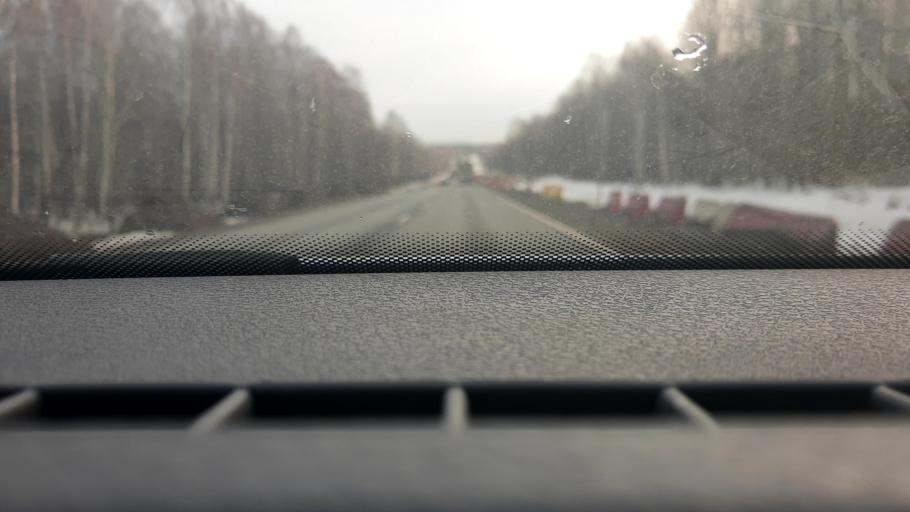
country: RU
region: Chelyabinsk
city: Asha
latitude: 54.8661
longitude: 57.1714
